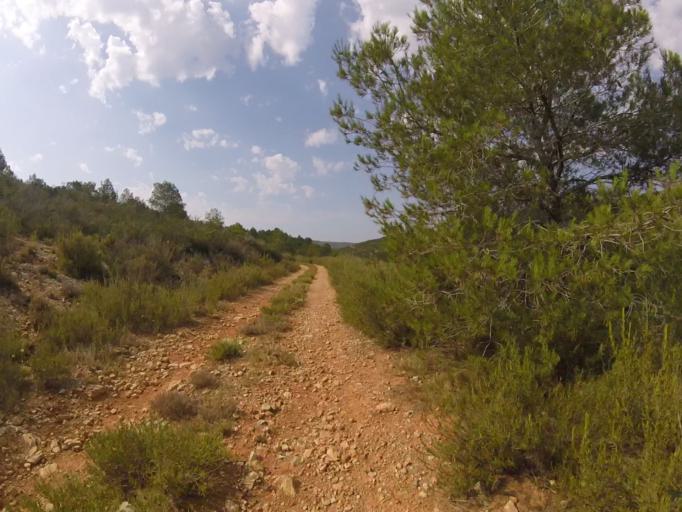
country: ES
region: Valencia
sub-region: Provincia de Castello
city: Alcala de Xivert
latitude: 40.3462
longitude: 0.1984
